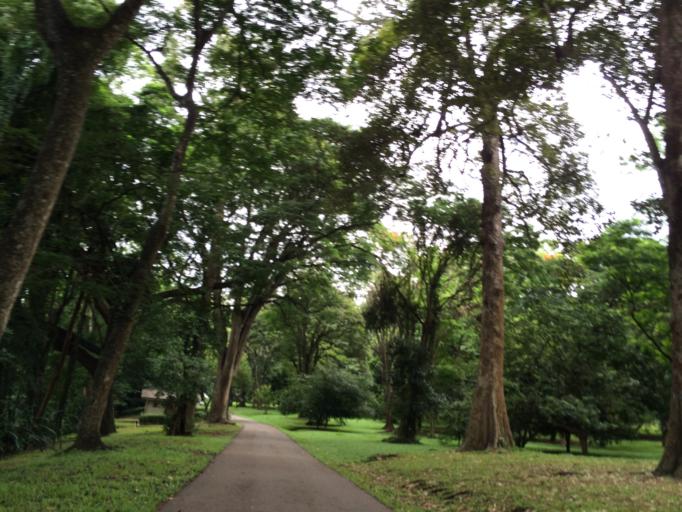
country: LK
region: Central
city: Kandy
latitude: 7.2726
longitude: 80.5936
